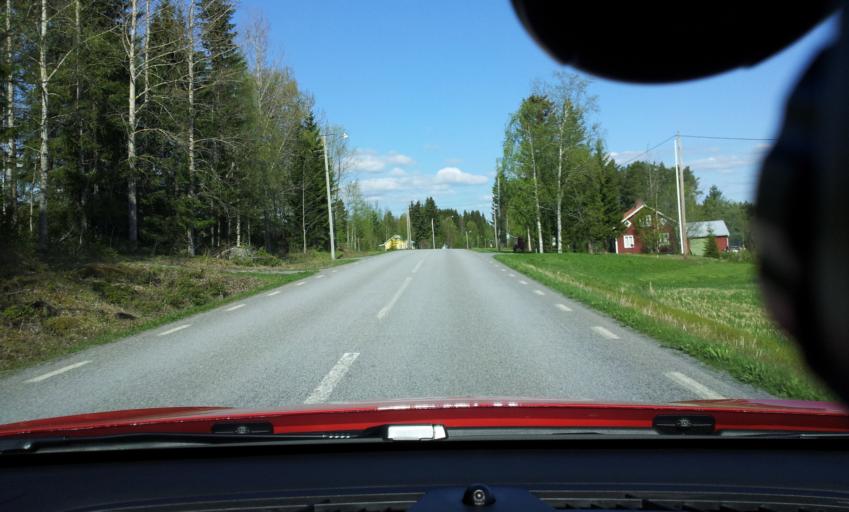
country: SE
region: Jaemtland
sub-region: Krokoms Kommun
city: Krokom
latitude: 63.1521
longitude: 14.1552
